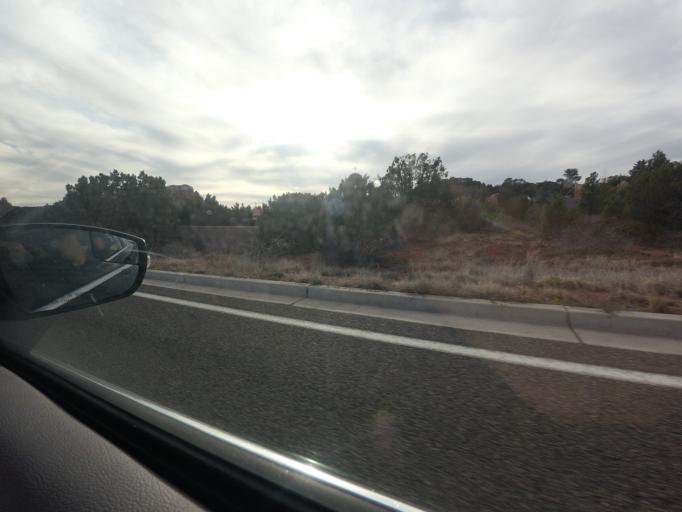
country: US
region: Arizona
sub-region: Coconino County
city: Sedona
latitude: 34.8308
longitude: -111.7777
